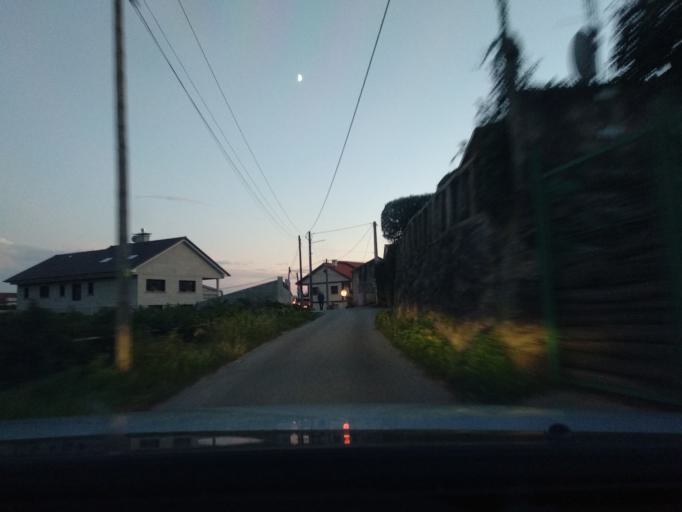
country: ES
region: Galicia
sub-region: Provincia de Pontevedra
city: Moana
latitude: 42.2874
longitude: -8.7510
